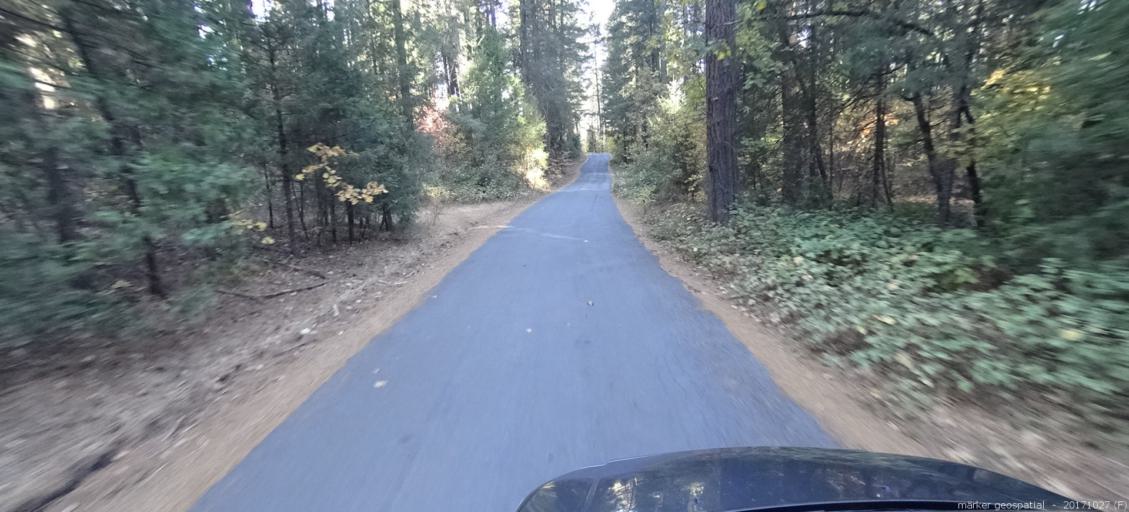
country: US
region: California
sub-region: Shasta County
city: Burney
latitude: 41.0040
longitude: -121.8918
